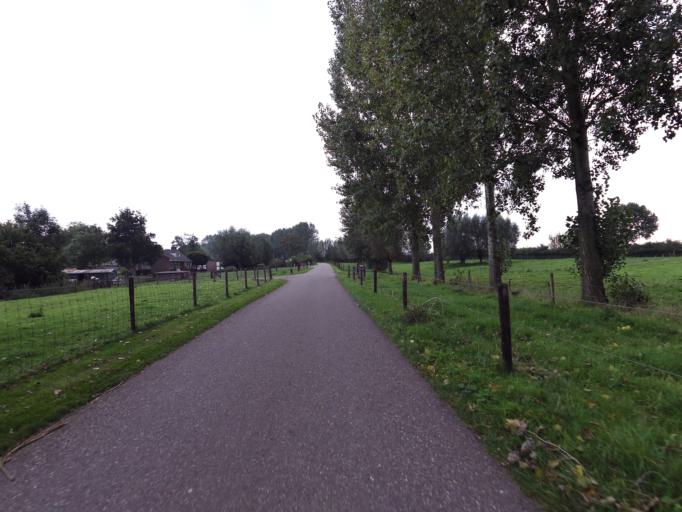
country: NL
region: Gelderland
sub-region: Gemeente Zevenaar
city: Zevenaar
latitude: 51.9099
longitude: 6.0956
